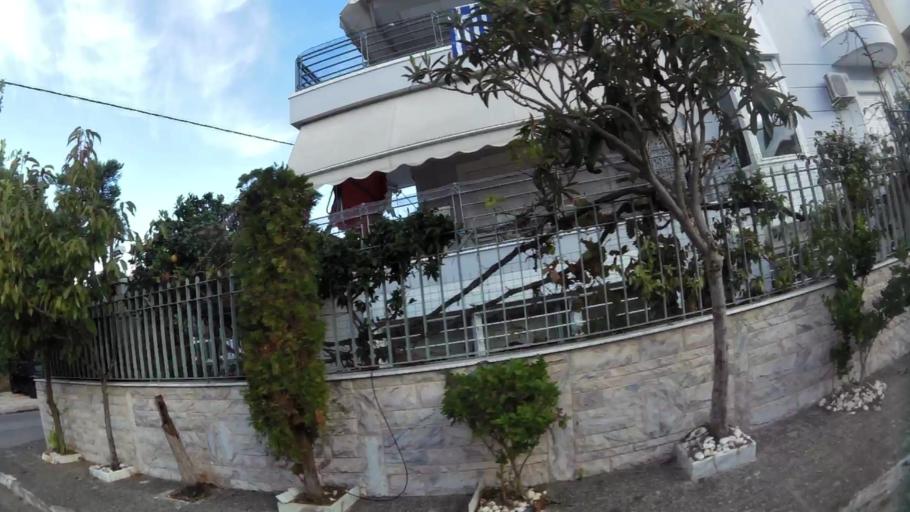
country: GR
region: Attica
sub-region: Nomarchia Athinas
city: Vrilissia
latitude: 38.0435
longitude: 23.8210
